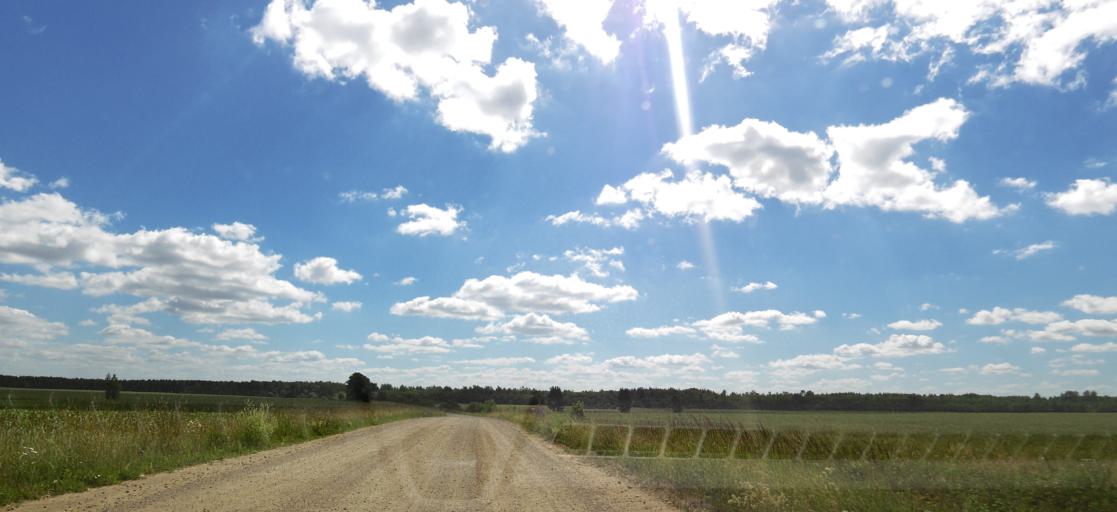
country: LT
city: Vabalninkas
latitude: 56.0095
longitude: 24.7913
